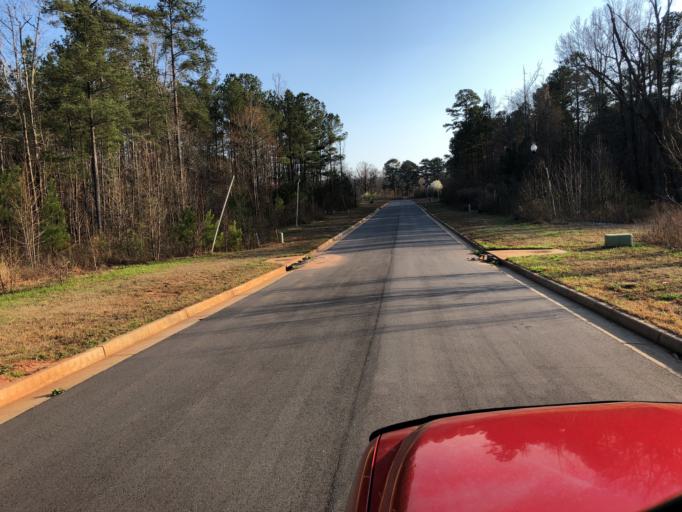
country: US
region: Georgia
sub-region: Henry County
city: McDonough
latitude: 33.4567
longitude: -84.1091
